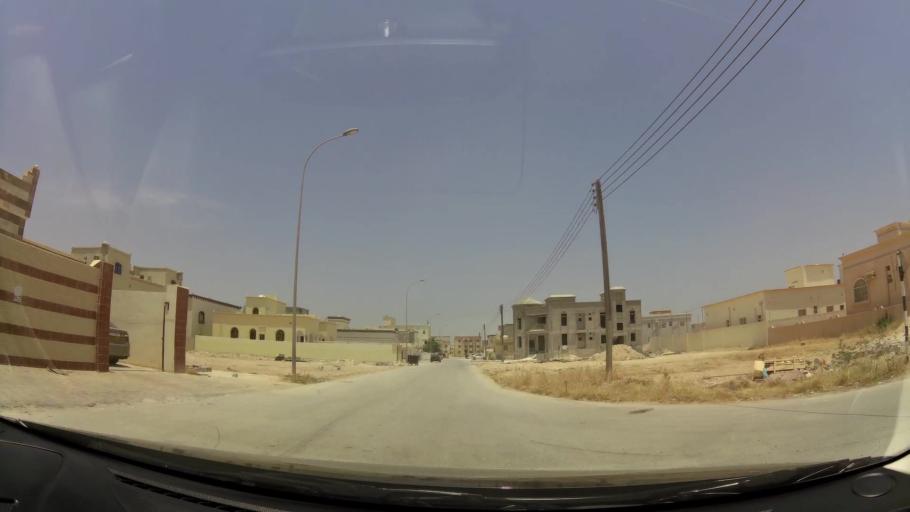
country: OM
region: Zufar
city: Salalah
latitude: 17.0814
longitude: 54.1620
